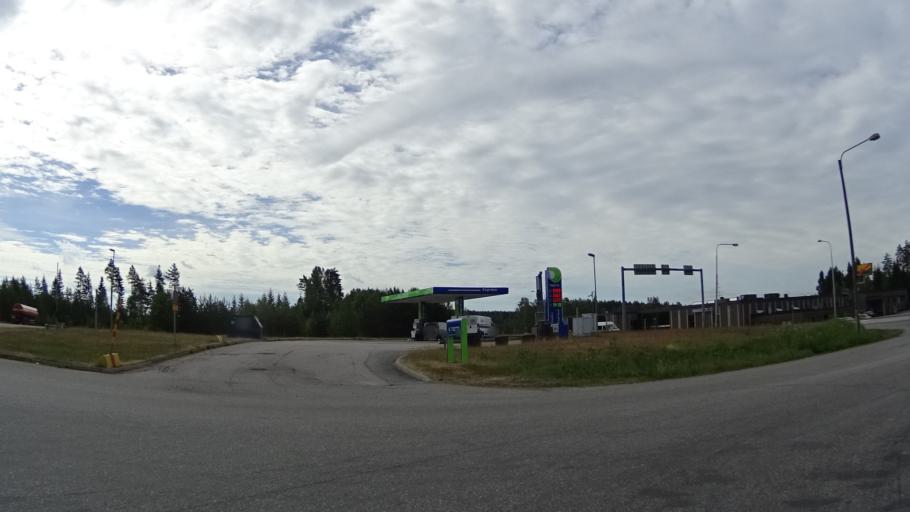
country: FI
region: Uusimaa
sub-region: Helsinki
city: Karkkila
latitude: 60.5183
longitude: 24.2466
